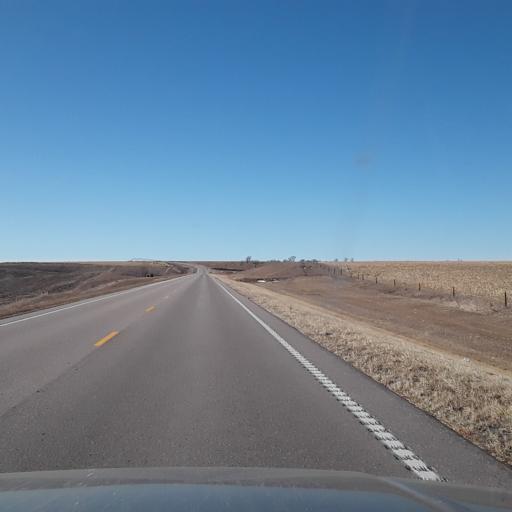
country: US
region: Nebraska
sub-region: Frontier County
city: Stockville
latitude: 40.7057
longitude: -100.2330
